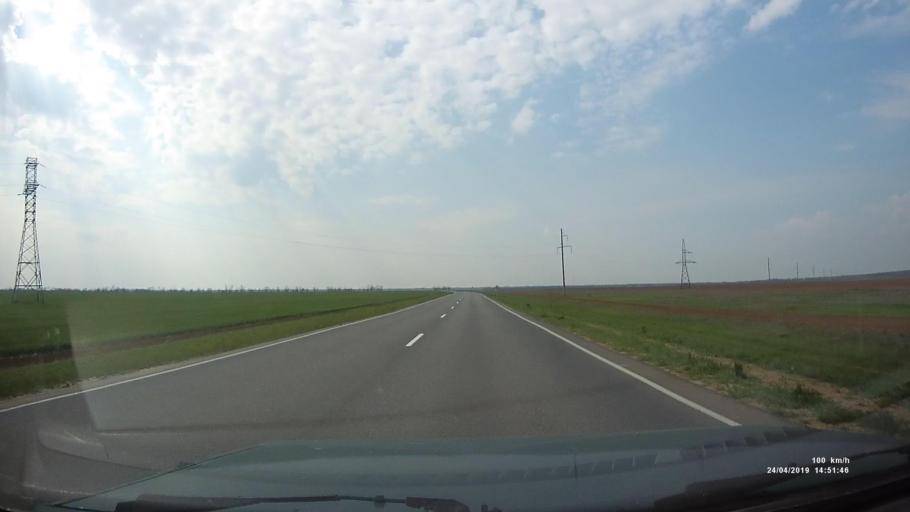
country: RU
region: Rostov
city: Remontnoye
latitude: 46.5274
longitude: 43.6943
